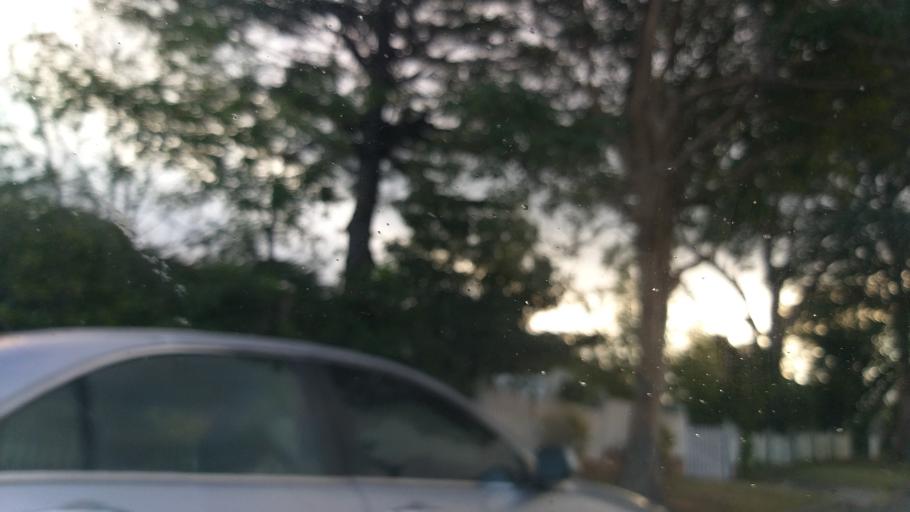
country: AU
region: New South Wales
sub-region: Wollongong
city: West Wollongong
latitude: -34.4241
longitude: 150.8634
